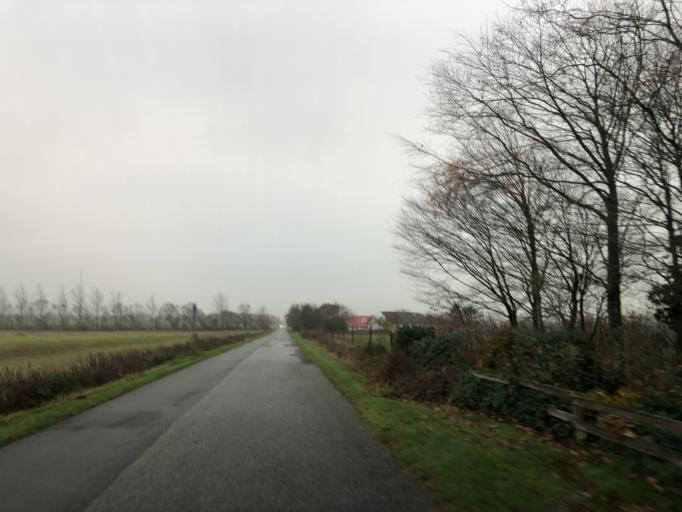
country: DK
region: Central Jutland
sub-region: Herning Kommune
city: Vildbjerg
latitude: 56.2183
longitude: 8.7651
